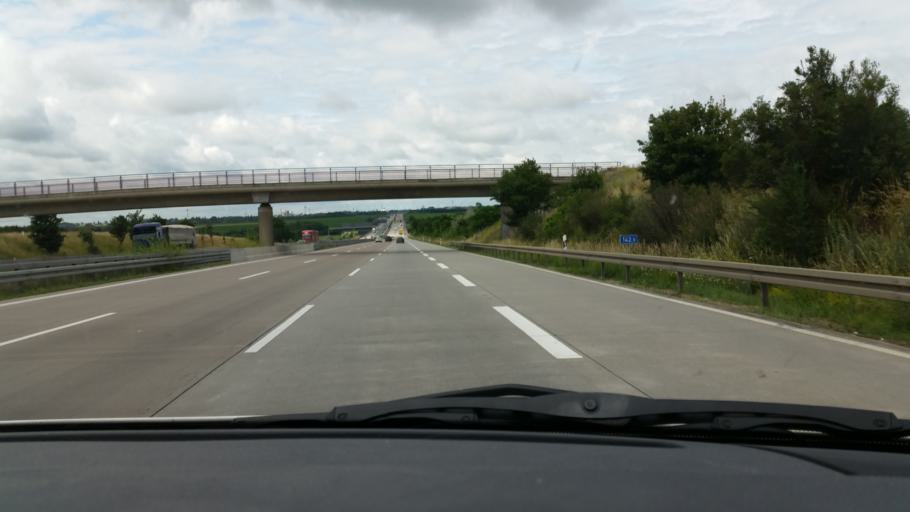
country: DE
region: Saxony-Anhalt
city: Grosskorbetha
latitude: 51.2325
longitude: 12.0543
